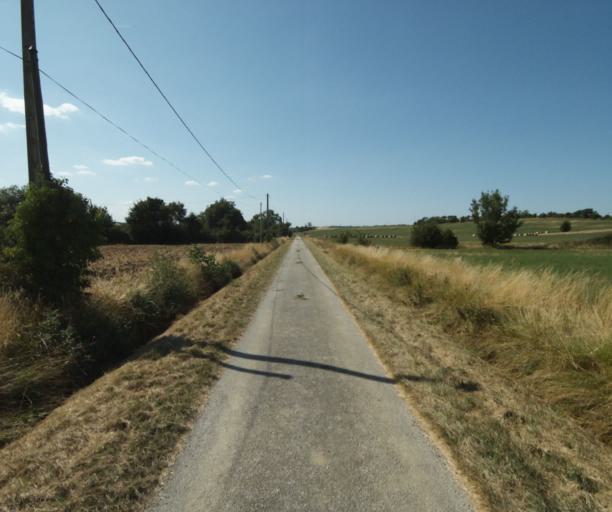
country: FR
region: Midi-Pyrenees
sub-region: Departement de la Haute-Garonne
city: Saint-Felix-Lauragais
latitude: 43.4744
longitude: 1.9052
